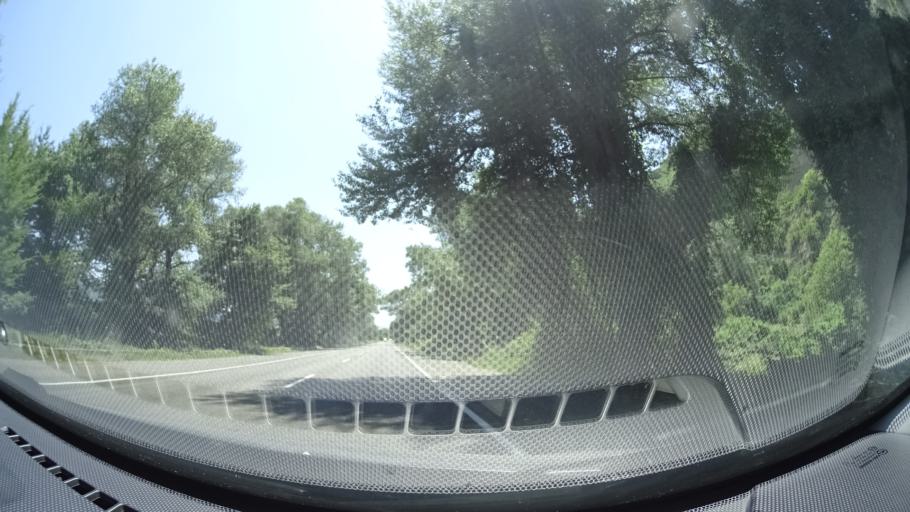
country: GE
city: Zhinvali
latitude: 42.0461
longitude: 44.7451
